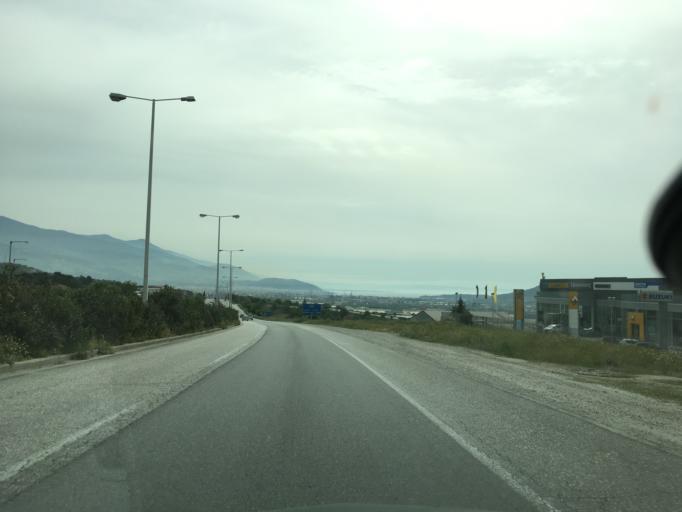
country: GR
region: Thessaly
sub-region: Nomos Magnisias
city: Nea Ionia
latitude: 39.3787
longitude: 22.8770
